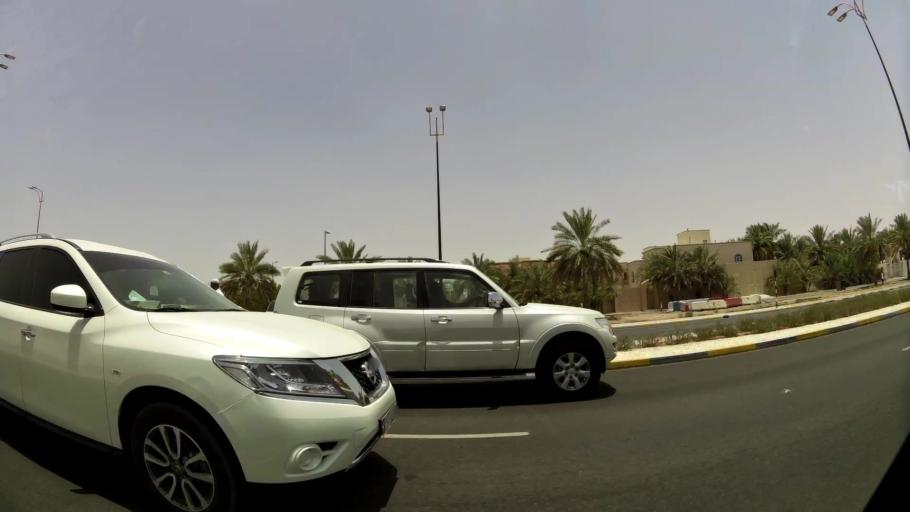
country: AE
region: Abu Dhabi
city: Al Ain
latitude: 24.2139
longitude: 55.7231
